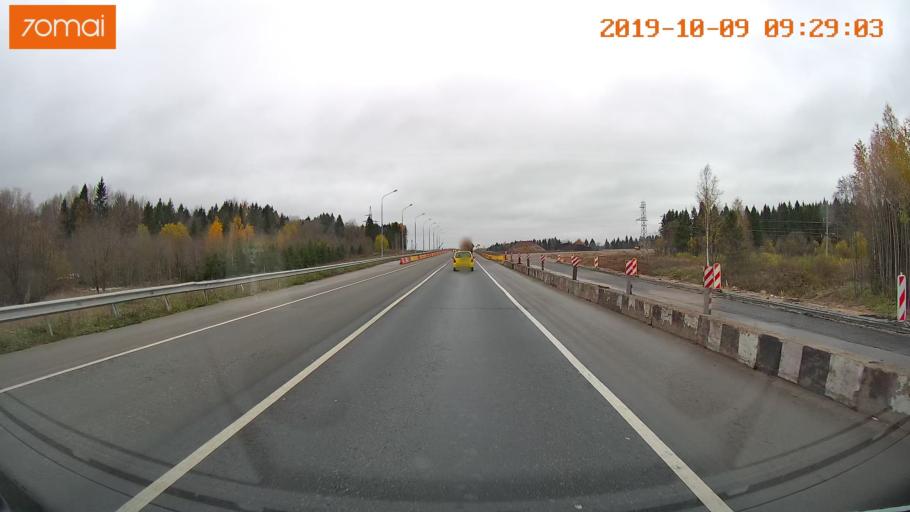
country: RU
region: Vologda
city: Vologda
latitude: 59.1285
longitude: 39.9615
